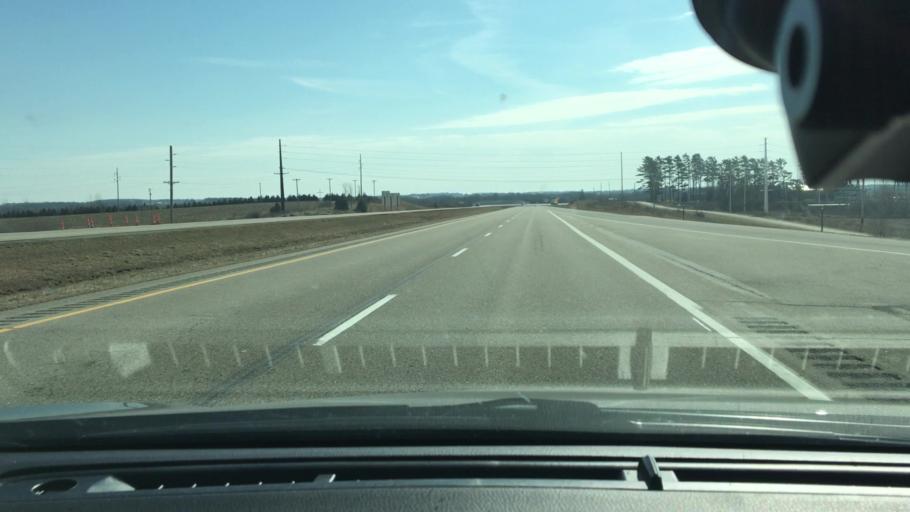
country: US
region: Iowa
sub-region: Floyd County
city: Charles City
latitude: 43.0387
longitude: -92.6682
